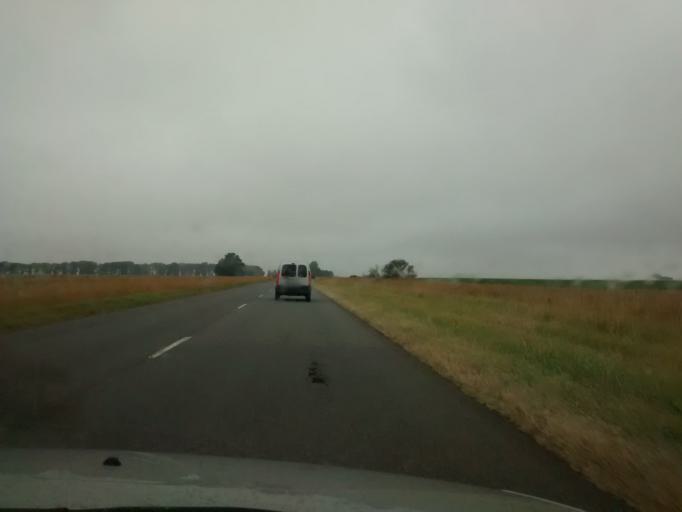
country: AR
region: Buenos Aires
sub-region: Partido de Ayacucho
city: Ayacucho
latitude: -37.4684
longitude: -58.4782
